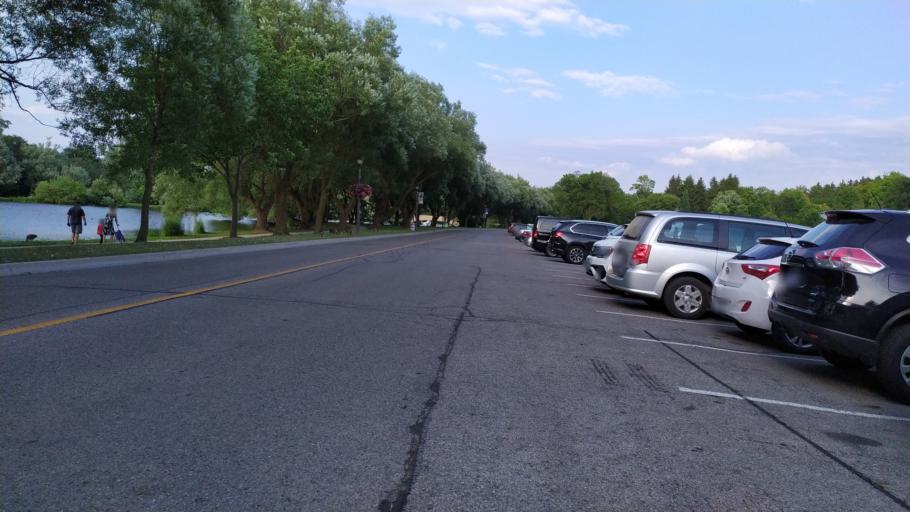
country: CA
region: Ontario
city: Stratford
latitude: 43.3757
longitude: -80.9688
